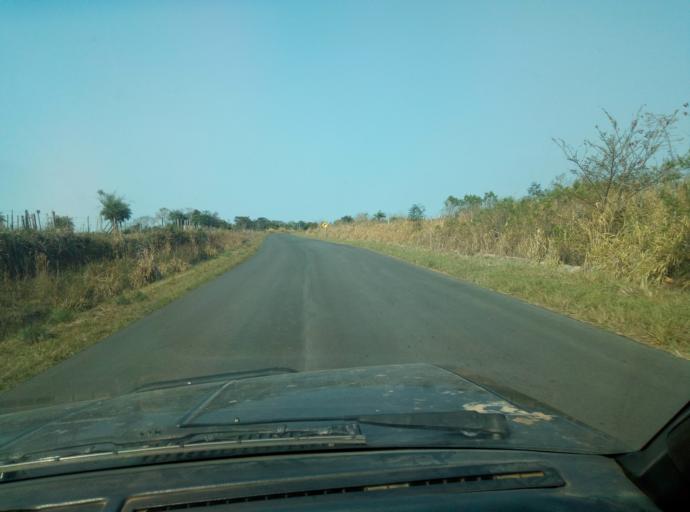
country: PY
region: Caaguazu
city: Carayao
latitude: -25.1835
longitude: -56.3124
